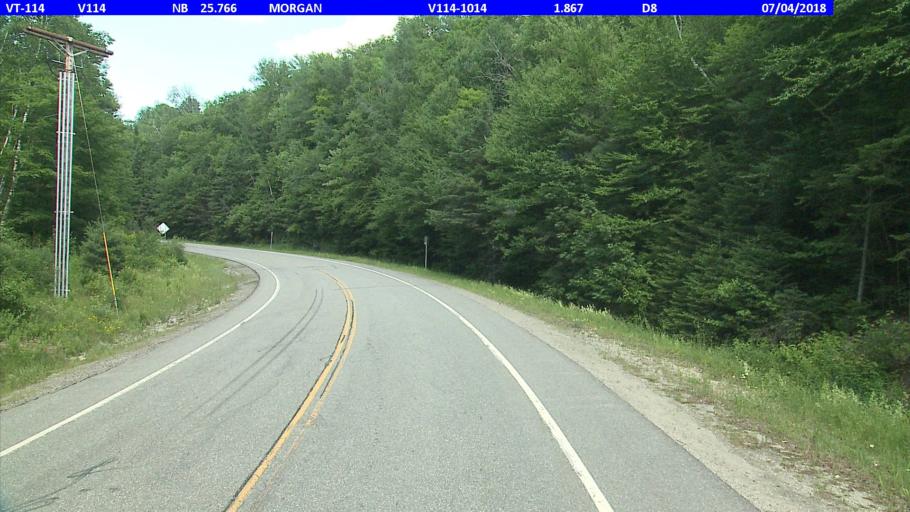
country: CA
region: Quebec
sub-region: Estrie
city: Coaticook
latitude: 44.8712
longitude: -71.9013
